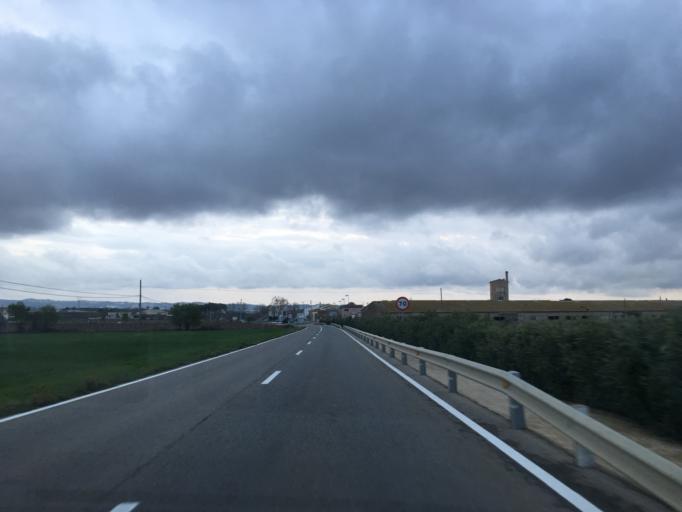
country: ES
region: Catalonia
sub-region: Provincia de Tarragona
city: Santa Oliva
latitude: 41.2868
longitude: 1.5258
